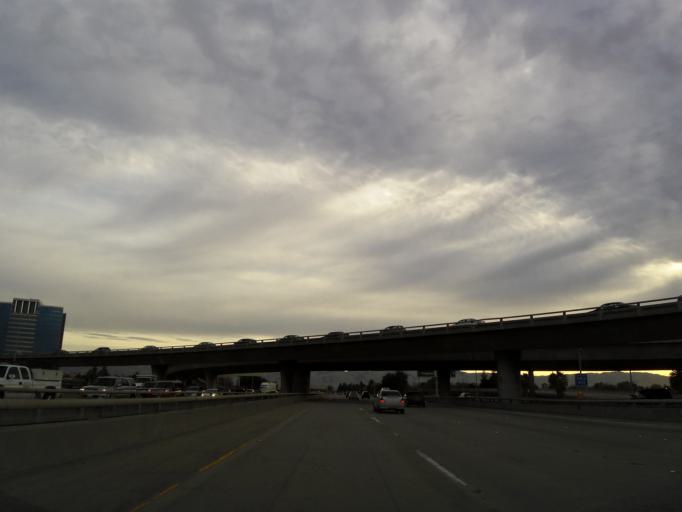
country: US
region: California
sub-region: Santa Clara County
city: San Jose
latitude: 37.3237
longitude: -121.8932
